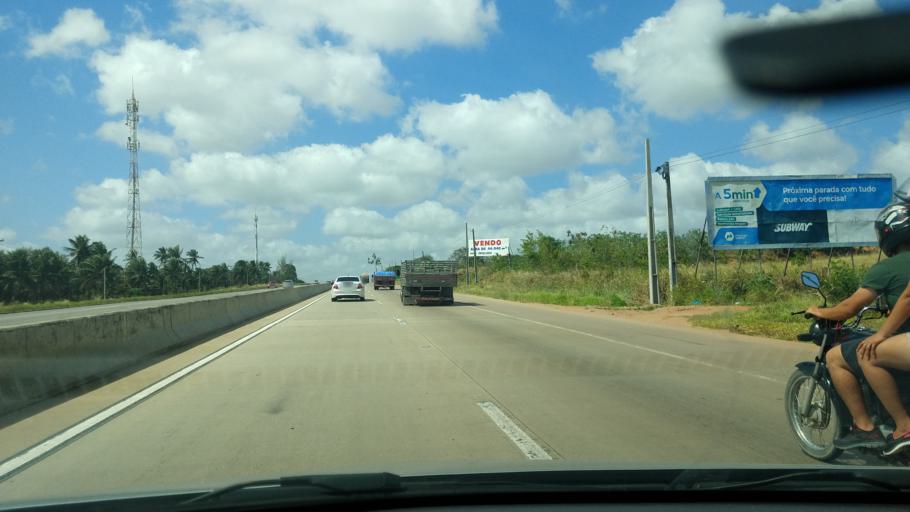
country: BR
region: Rio Grande do Norte
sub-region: Parnamirim
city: Parnamirim
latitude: -5.9482
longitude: -35.2648
